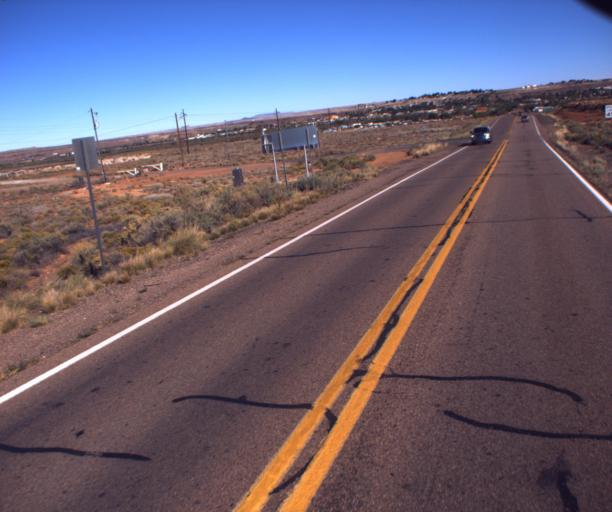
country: US
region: Arizona
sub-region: Navajo County
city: Holbrook
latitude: 34.8861
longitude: -110.1626
